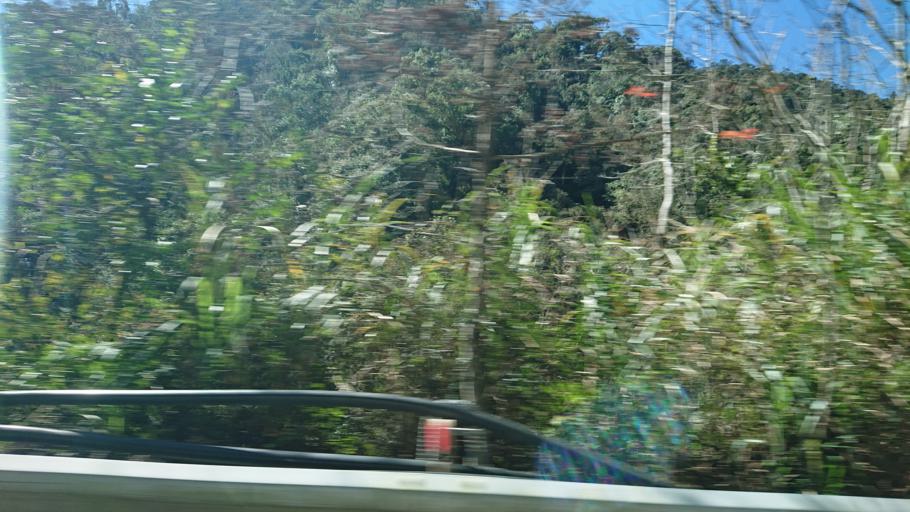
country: TW
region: Taiwan
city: Daxi
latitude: 24.4127
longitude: 121.3592
